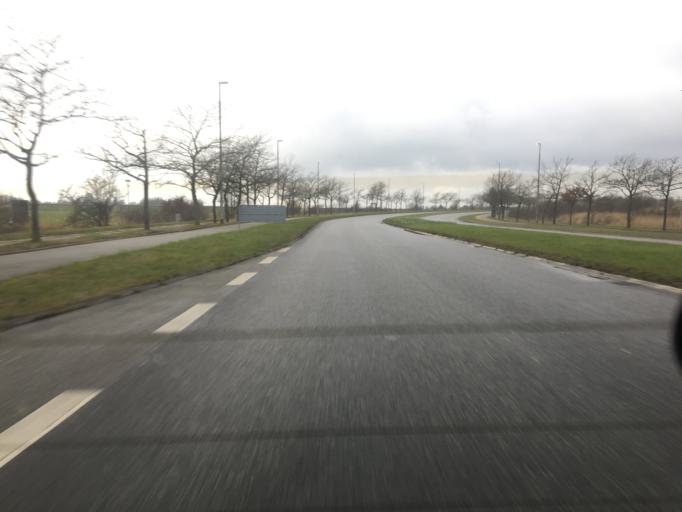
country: DK
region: Capital Region
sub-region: Hvidovre Kommune
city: Hvidovre
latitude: 55.6137
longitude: 12.4484
